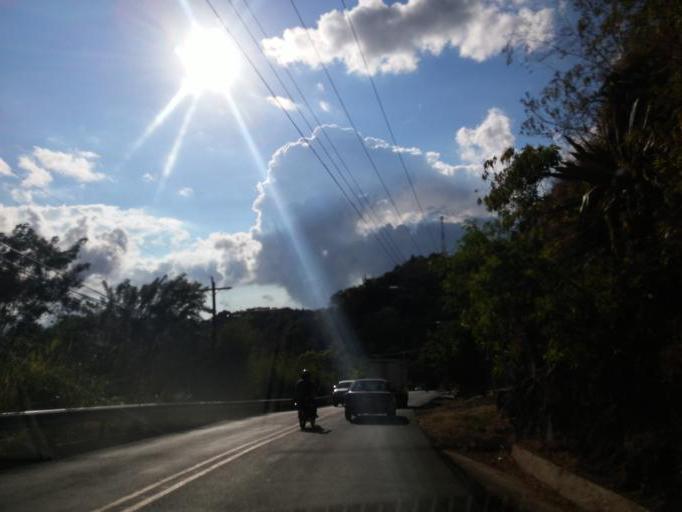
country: CR
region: San Jose
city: San Ignacio
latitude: 9.7960
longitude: -84.1537
